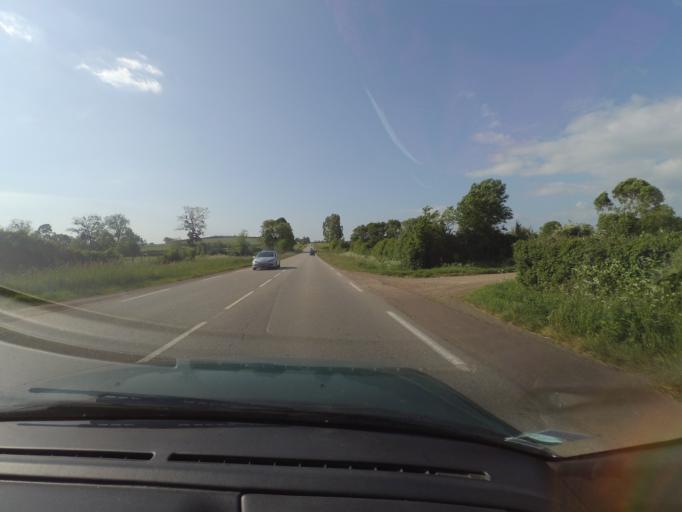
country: FR
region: Pays de la Loire
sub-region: Departement de la Vendee
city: Angles
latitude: 46.4375
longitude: -1.4037
